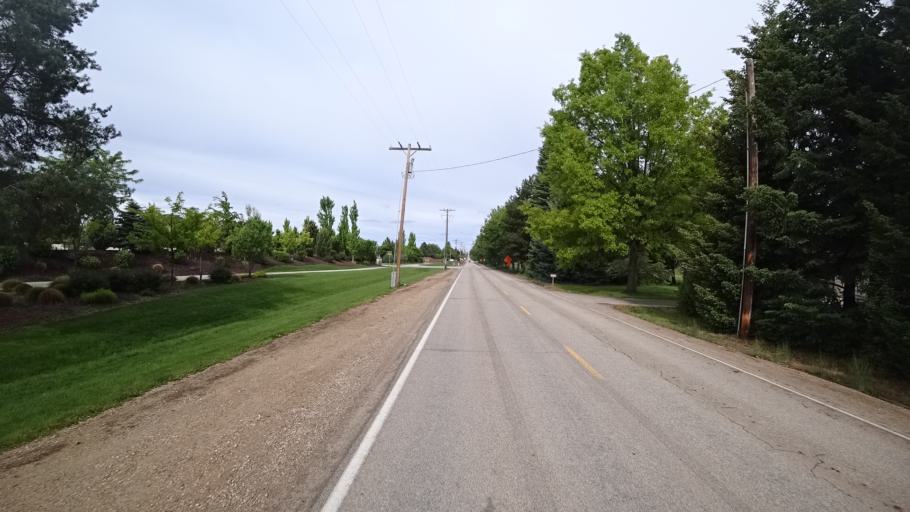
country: US
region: Idaho
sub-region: Ada County
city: Eagle
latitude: 43.7208
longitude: -116.3992
